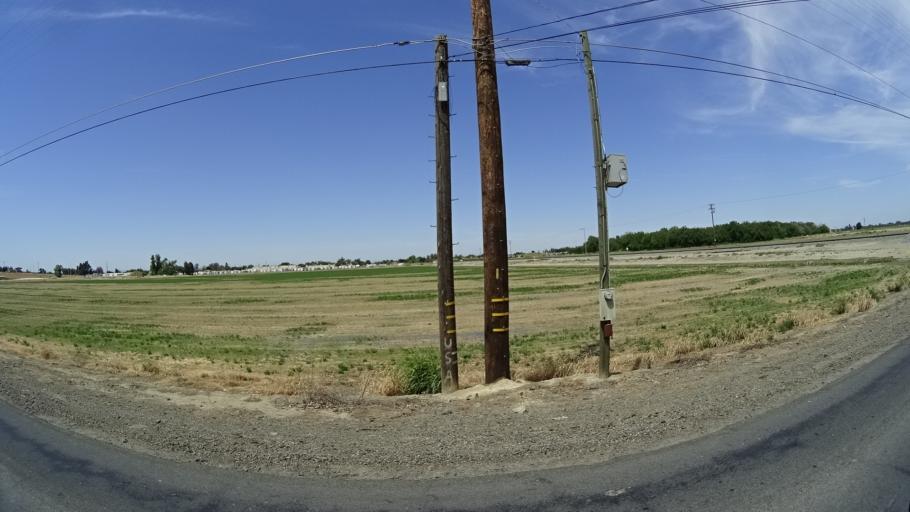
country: US
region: California
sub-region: Kings County
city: Armona
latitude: 36.3173
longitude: -119.6910
